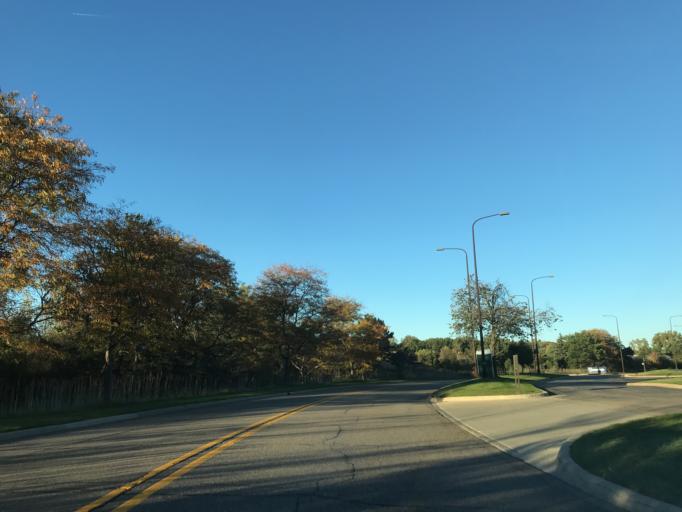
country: US
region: Michigan
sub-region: Oakland County
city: Clawson
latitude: 42.5656
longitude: -83.1575
